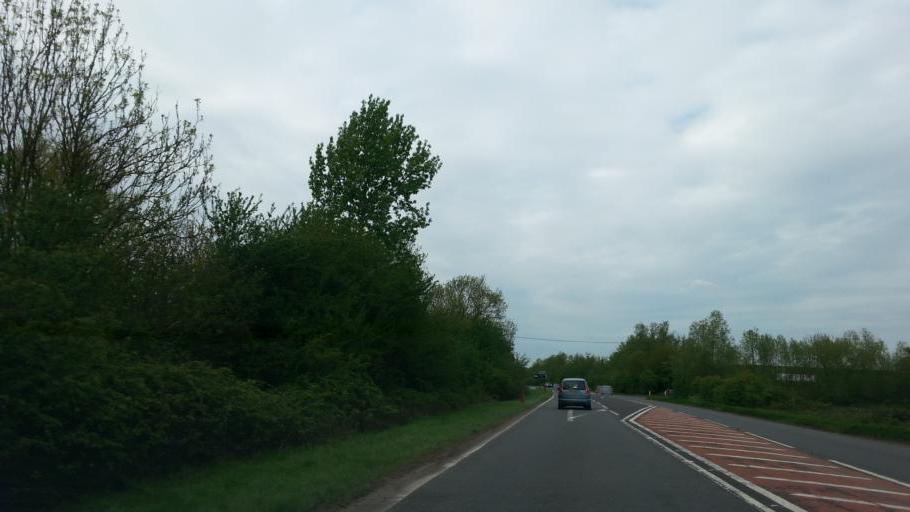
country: GB
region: England
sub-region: Cambridgeshire
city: March
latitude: 52.5157
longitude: 0.0904
